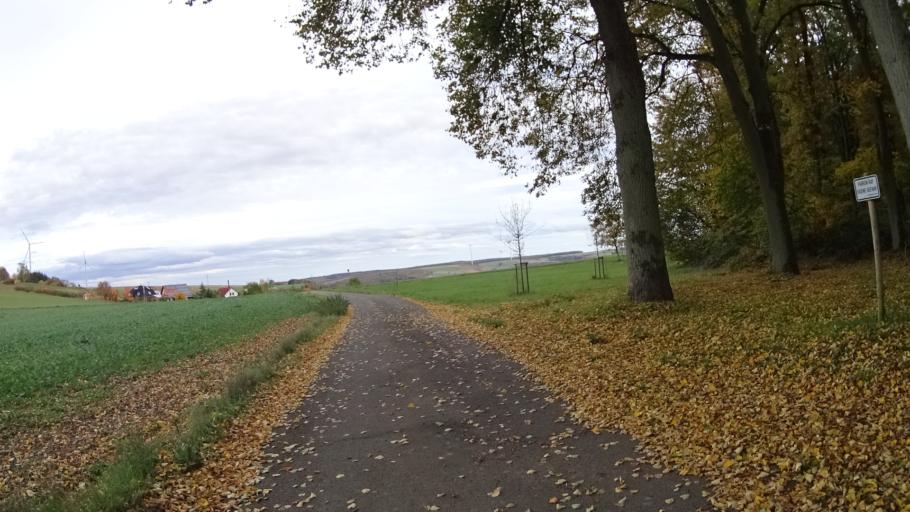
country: DE
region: Rheinland-Pfalz
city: Winterborn
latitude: 49.7429
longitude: 7.8567
